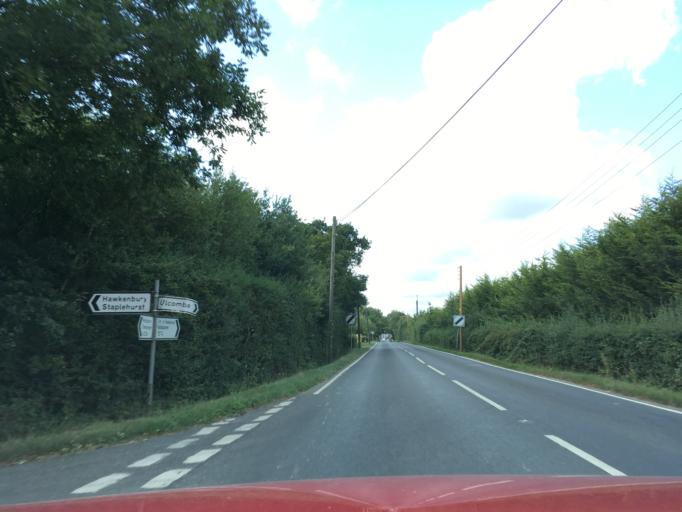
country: GB
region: England
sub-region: Kent
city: Headcorn
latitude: 51.1787
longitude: 0.6126
